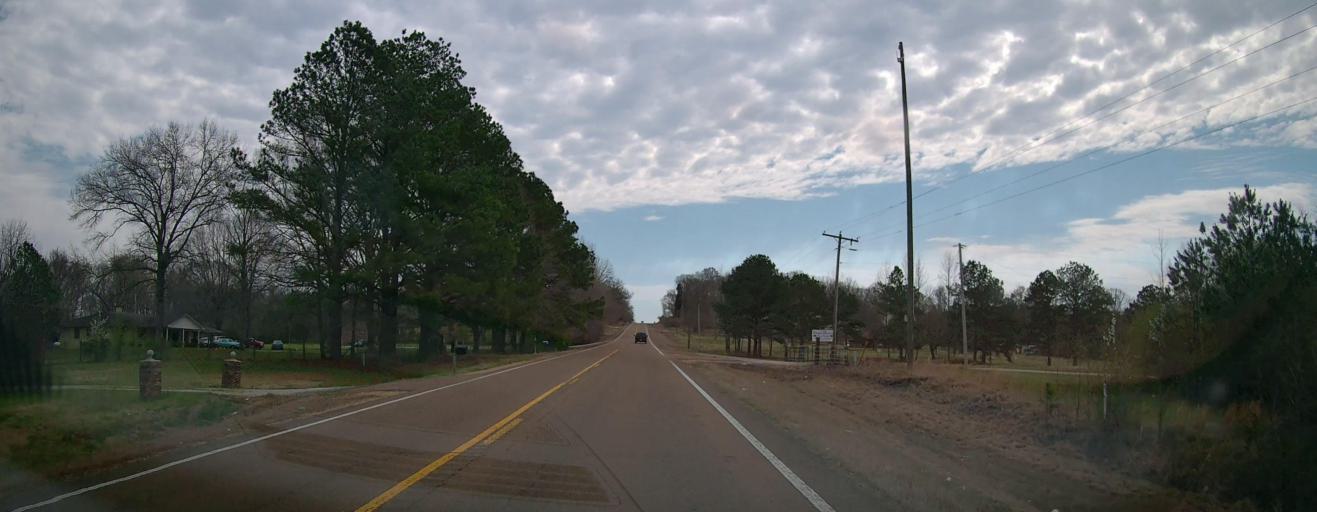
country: US
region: Mississippi
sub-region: Marshall County
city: Byhalia
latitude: 34.8452
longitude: -89.6150
